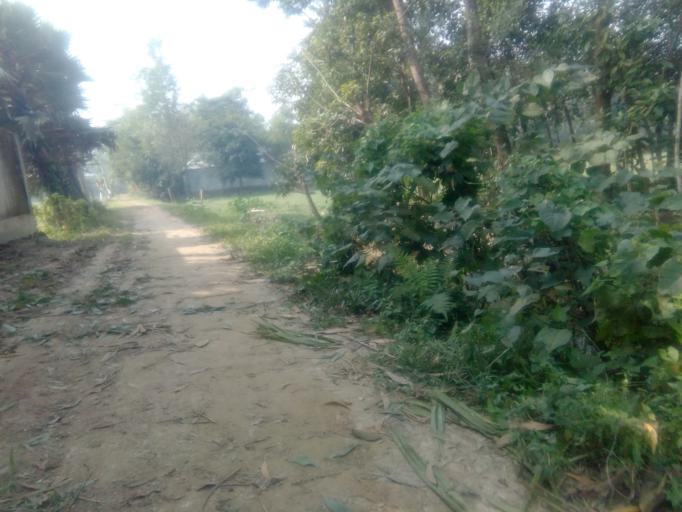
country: IN
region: Tripura
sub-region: West Tripura
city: Sonamura
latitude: 23.3204
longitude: 91.2798
